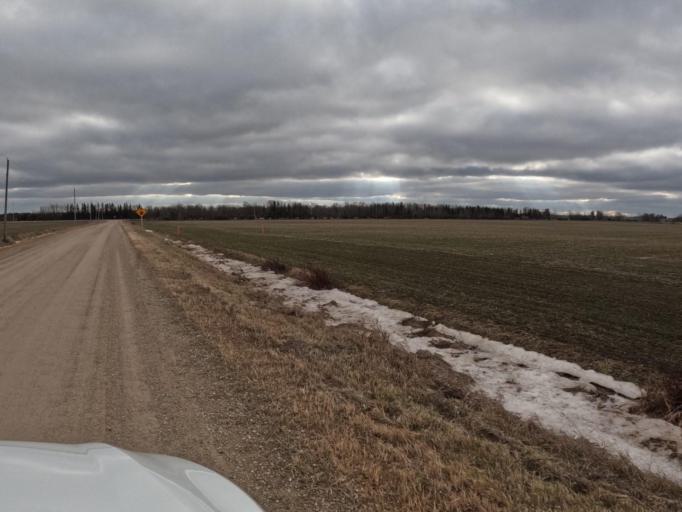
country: CA
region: Ontario
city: Shelburne
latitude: 43.8598
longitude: -80.3996
